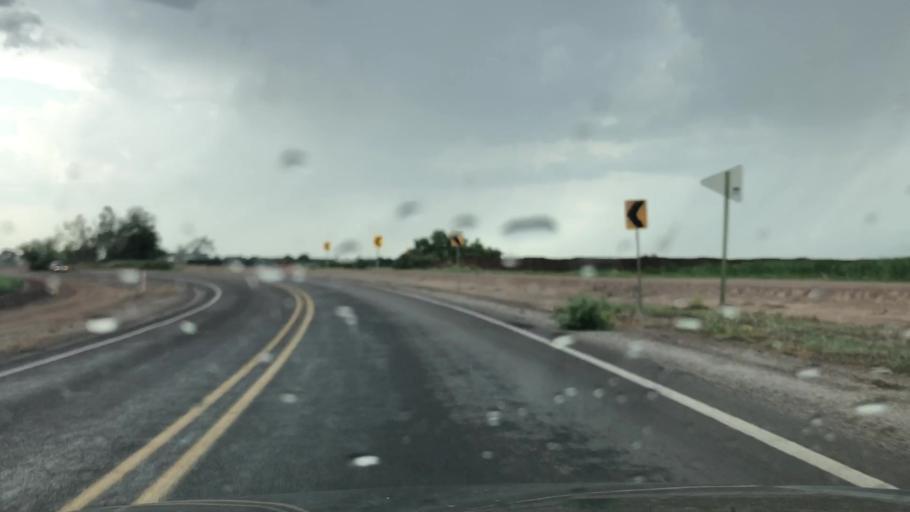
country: US
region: New Mexico
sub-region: Dona Ana County
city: Vado
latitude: 32.0676
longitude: -106.6796
